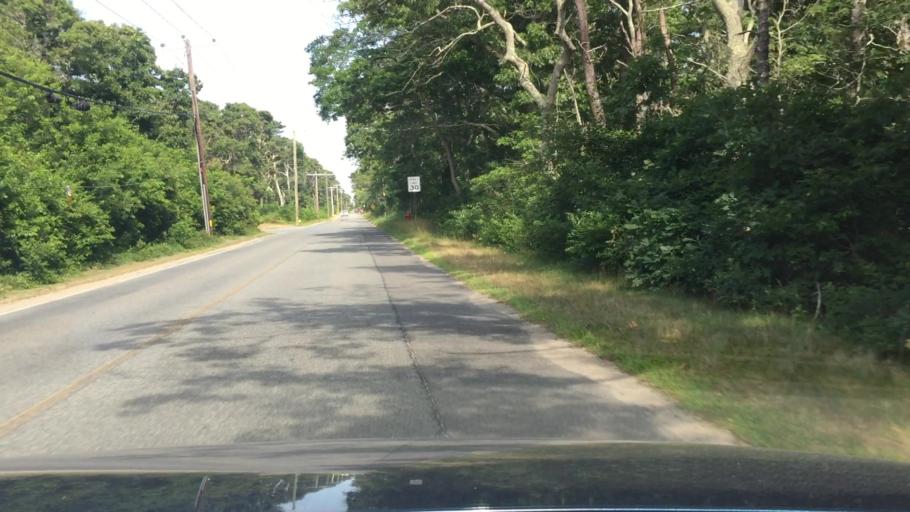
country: US
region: Massachusetts
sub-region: Barnstable County
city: North Eastham
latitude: 41.8574
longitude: -69.9702
